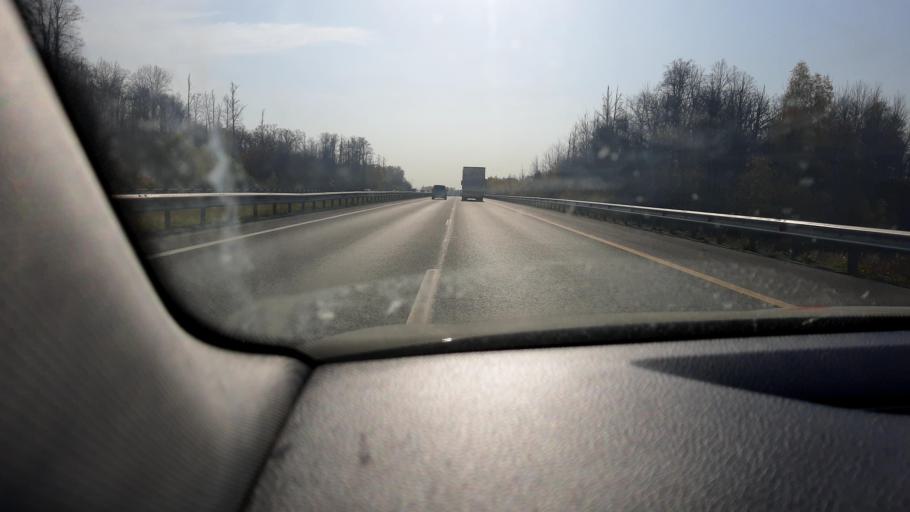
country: RU
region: Moskovskaya
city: Zhilevo
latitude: 55.0035
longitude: 37.9567
